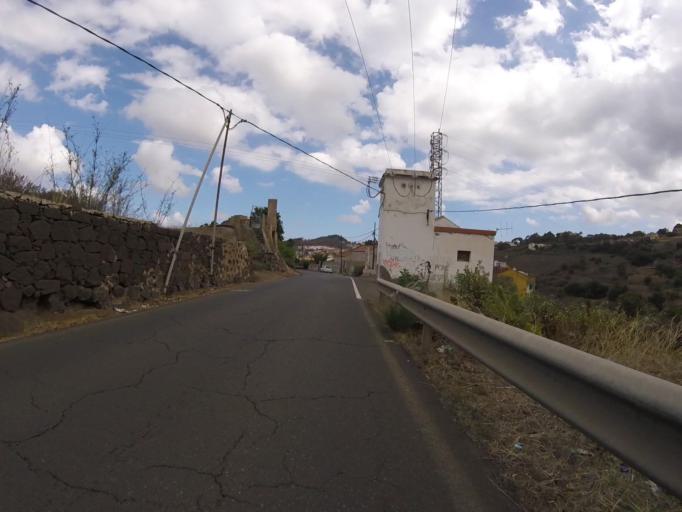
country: ES
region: Canary Islands
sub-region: Provincia de Las Palmas
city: Santa Brigida
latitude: 28.0449
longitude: -15.4857
